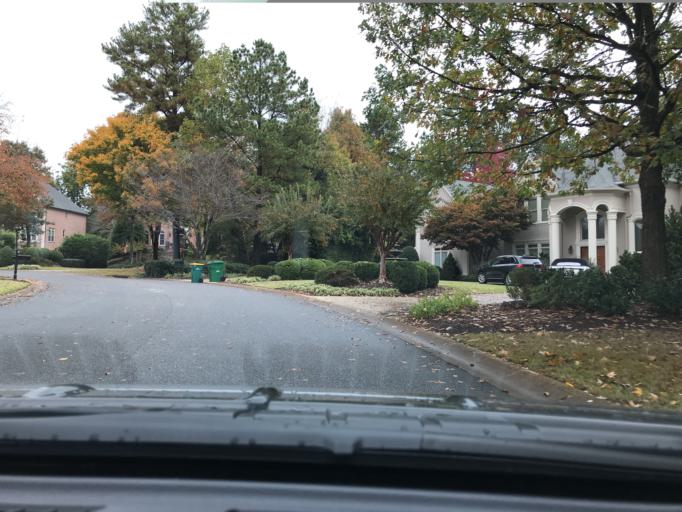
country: US
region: Georgia
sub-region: Fulton County
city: Johns Creek
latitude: 34.0141
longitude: -84.2463
